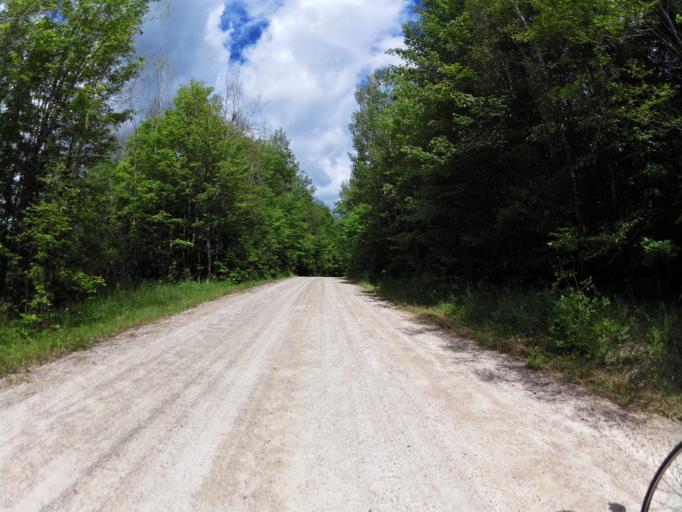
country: CA
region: Ontario
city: Perth
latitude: 45.0262
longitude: -76.5161
